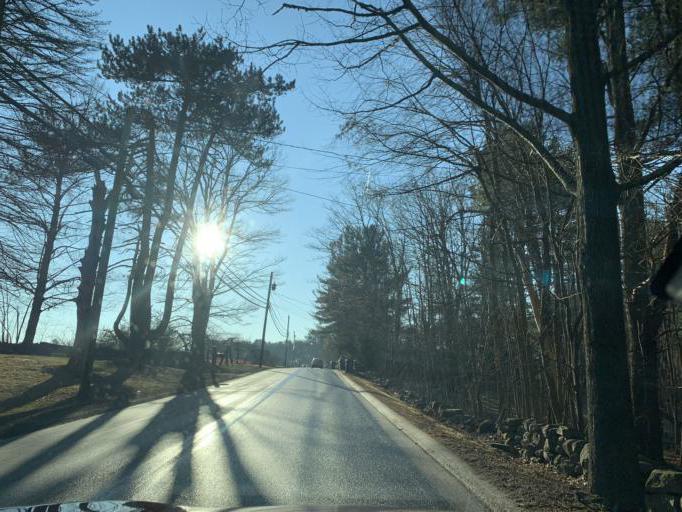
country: US
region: New Hampshire
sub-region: Rockingham County
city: Londonderry
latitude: 42.8713
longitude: -71.3566
